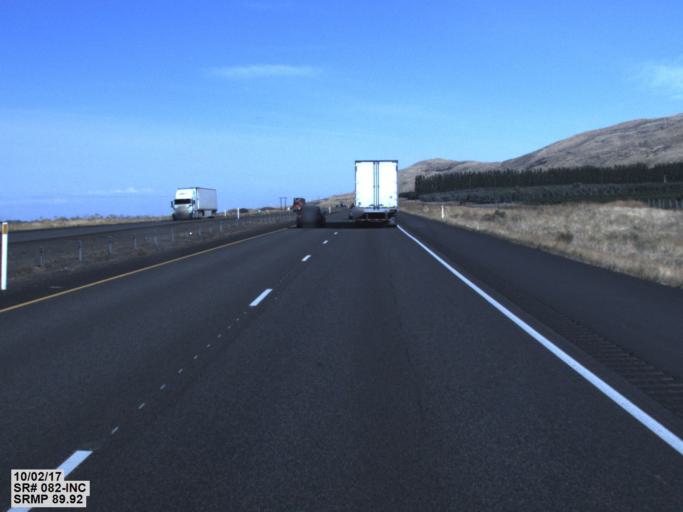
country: US
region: Washington
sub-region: Benton County
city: Benton City
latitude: 46.2528
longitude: -119.6065
